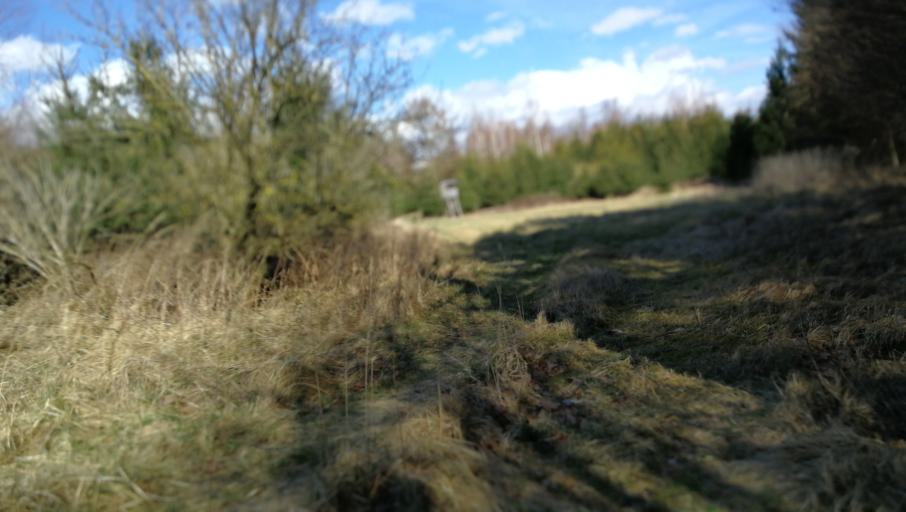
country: DE
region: Bavaria
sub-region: Upper Bavaria
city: Landsberied
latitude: 48.1994
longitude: 11.1993
